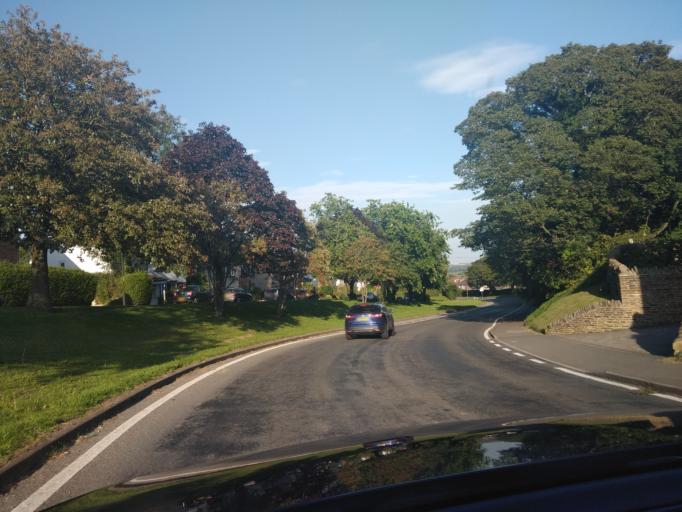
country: GB
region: England
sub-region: Derbyshire
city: Dronfield
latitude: 53.2957
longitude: -1.5164
